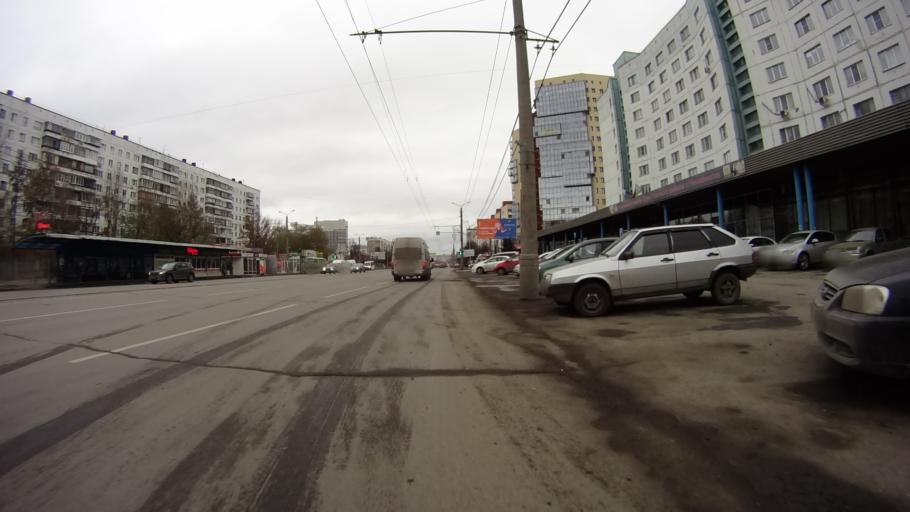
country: RU
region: Chelyabinsk
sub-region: Gorod Chelyabinsk
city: Chelyabinsk
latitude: 55.1944
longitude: 61.3395
